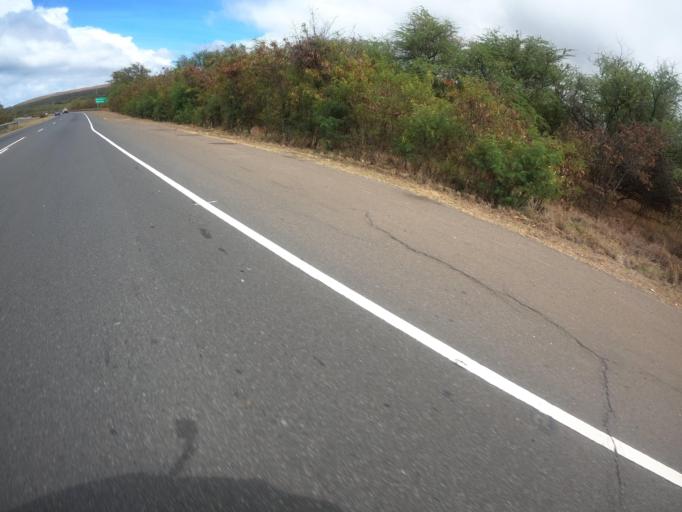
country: US
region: Hawaii
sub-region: Honolulu County
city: Makakilo City
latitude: 21.3351
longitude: -158.0945
